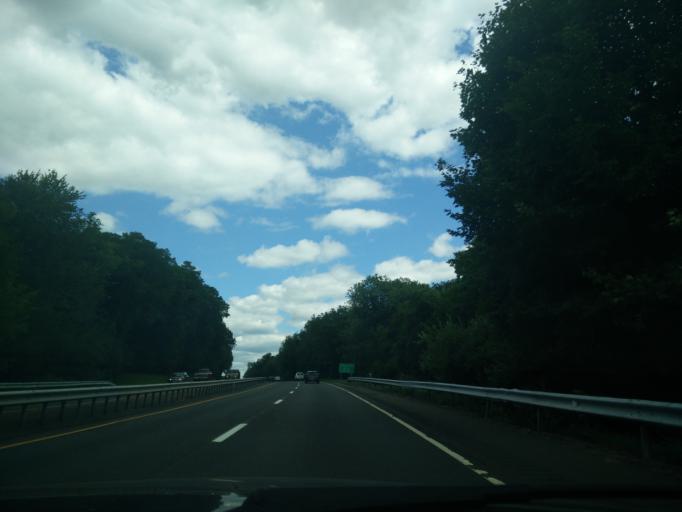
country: US
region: Connecticut
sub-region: New Haven County
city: Hamden
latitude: 41.3612
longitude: -72.9338
